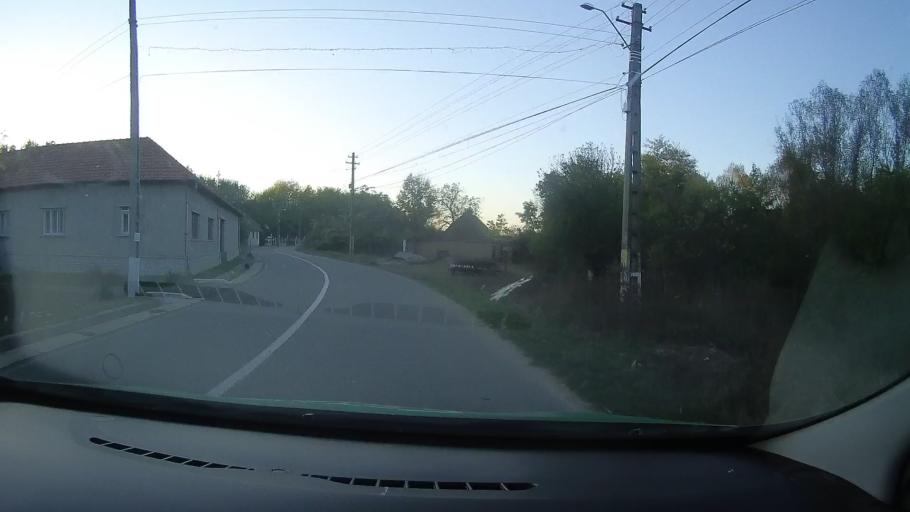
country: RO
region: Timis
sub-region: Comuna Traian Vuia
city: Traian Vuia
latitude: 45.7633
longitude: 22.0969
